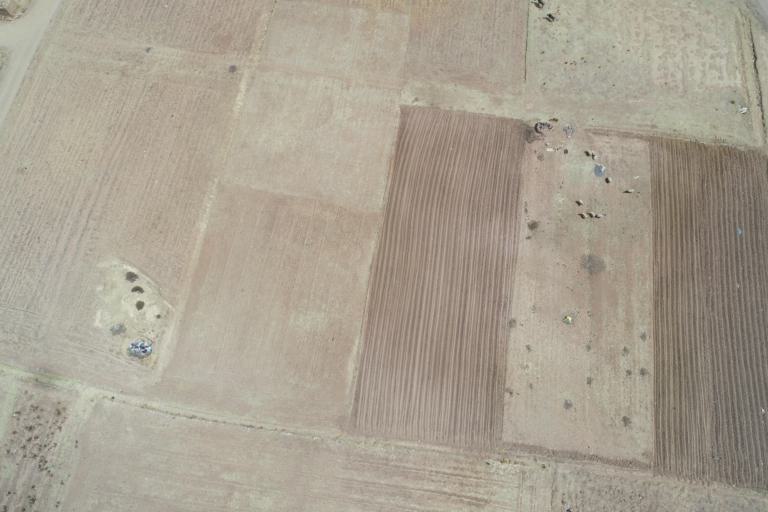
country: BO
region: La Paz
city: Achacachi
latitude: -15.9137
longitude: -68.8856
